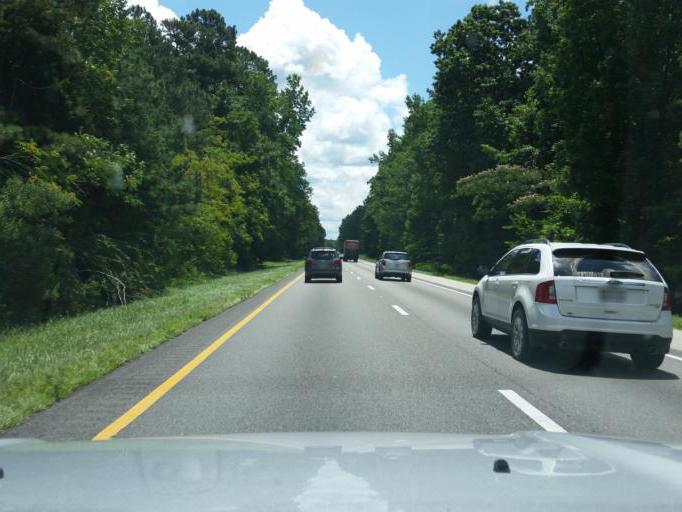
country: US
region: Virginia
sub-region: City of Williamsburg
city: Williamsburg
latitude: 37.3290
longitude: -76.7050
